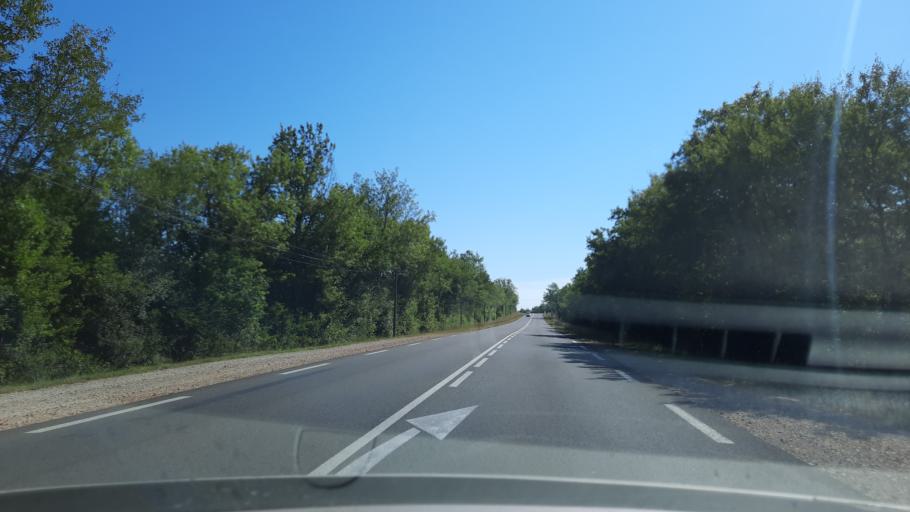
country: FR
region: Midi-Pyrenees
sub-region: Departement du Tarn-et-Garonne
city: Septfonds
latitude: 44.1963
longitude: 1.6907
